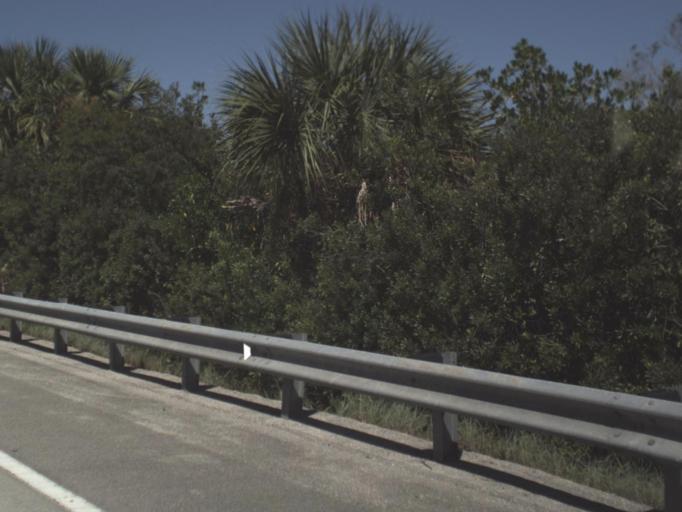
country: US
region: Florida
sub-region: Collier County
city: Marco
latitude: 25.9694
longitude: -81.5402
